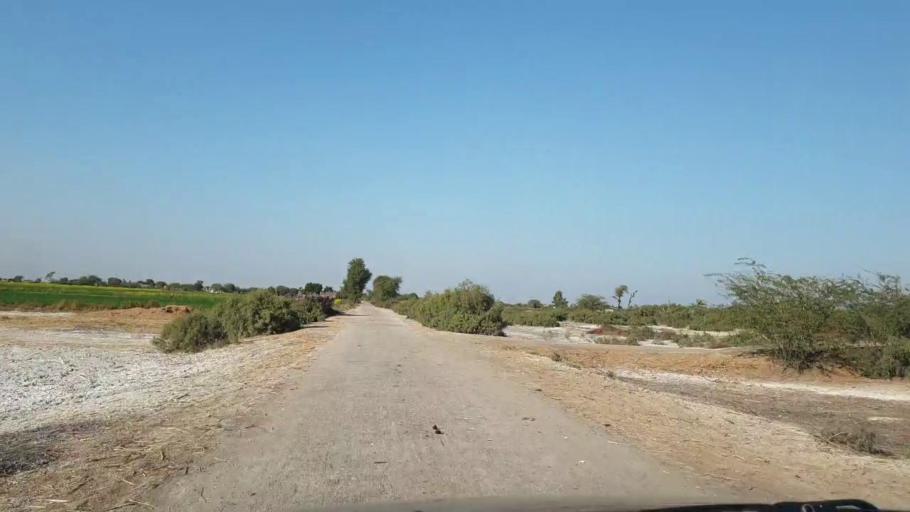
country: PK
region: Sindh
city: Khadro
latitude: 26.2079
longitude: 68.7543
